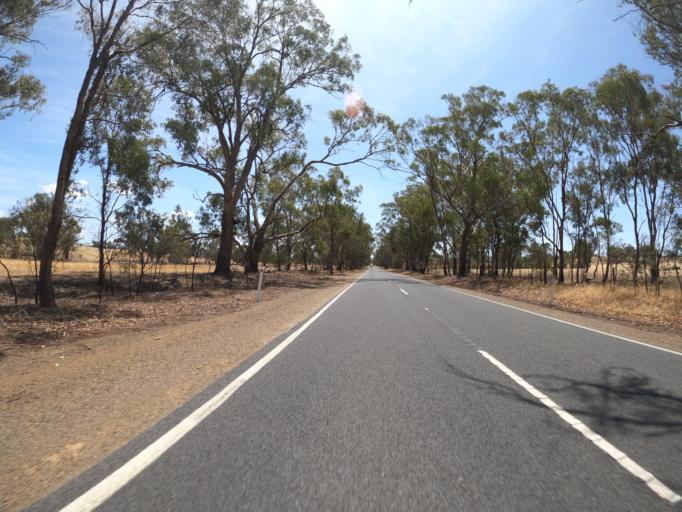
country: AU
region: Victoria
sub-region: Benalla
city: Benalla
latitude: -36.3672
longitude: 145.9706
